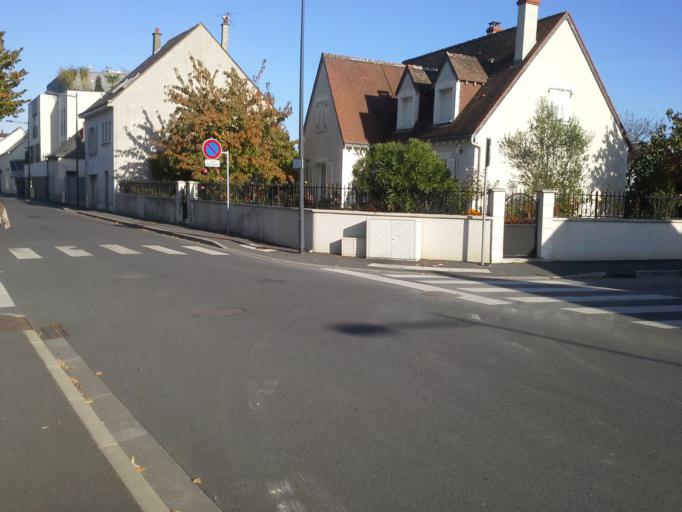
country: FR
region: Centre
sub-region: Departement d'Indre-et-Loire
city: La Riche
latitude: 47.3881
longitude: 0.6625
